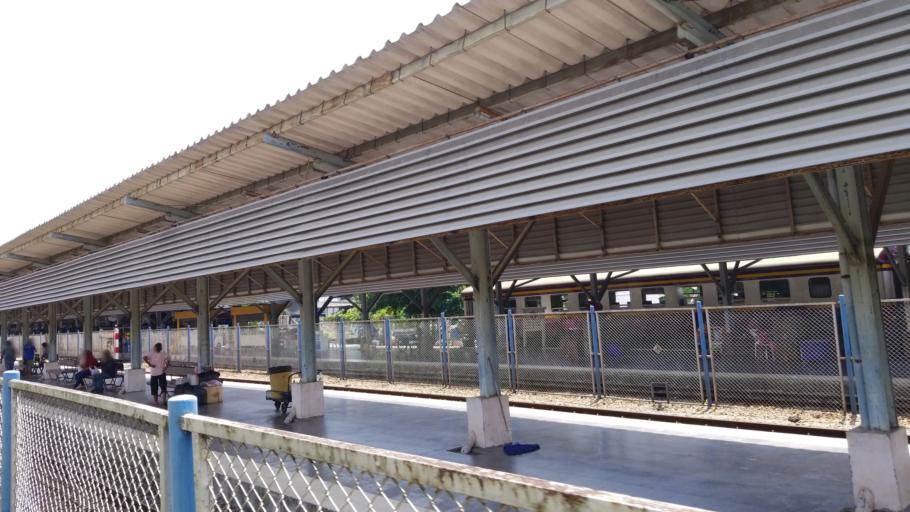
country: TH
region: Songkhla
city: Hat Yai
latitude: 7.0026
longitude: 100.4674
